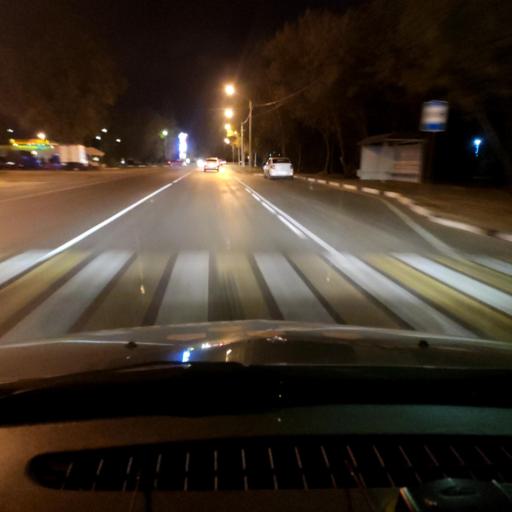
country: RU
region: Voronezj
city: Voronezh
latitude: 51.6184
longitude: 39.1771
